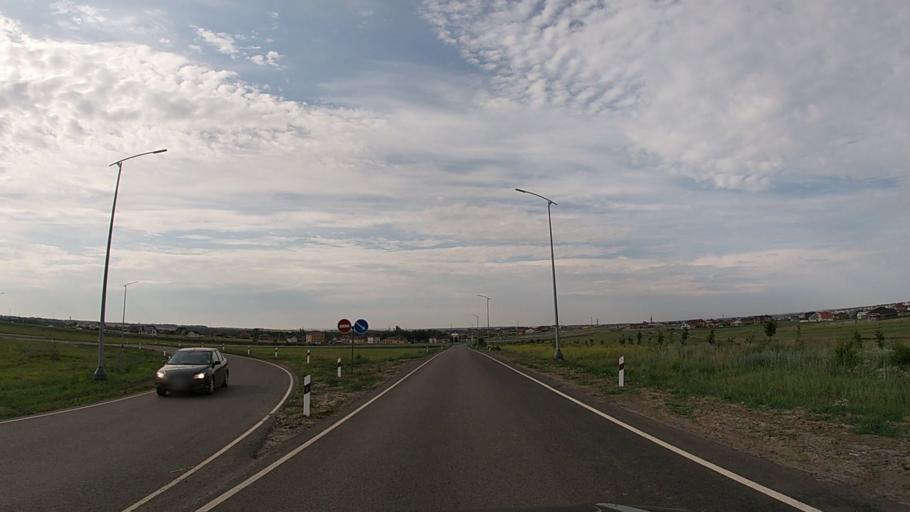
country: RU
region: Belgorod
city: Severnyy
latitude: 50.6742
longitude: 36.4700
